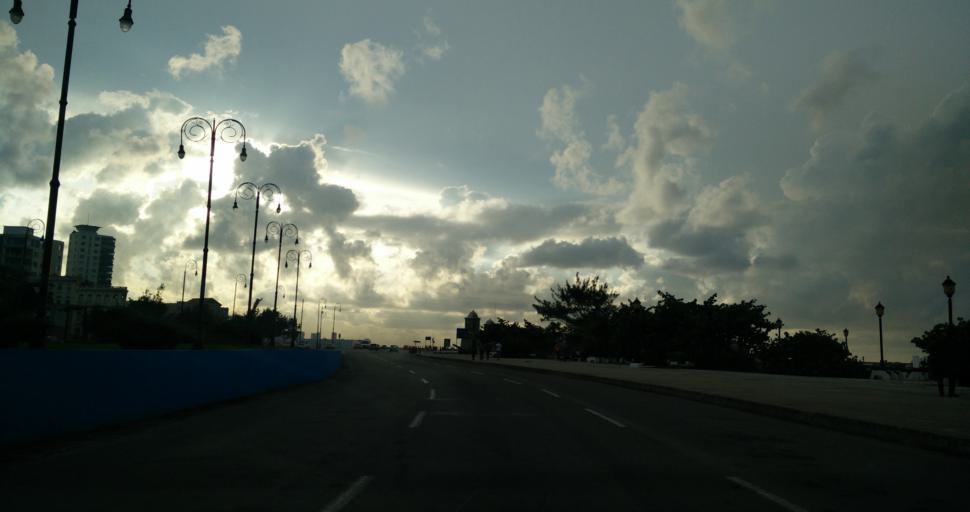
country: CU
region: La Habana
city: Centro Habana
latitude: 23.1455
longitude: -82.3557
